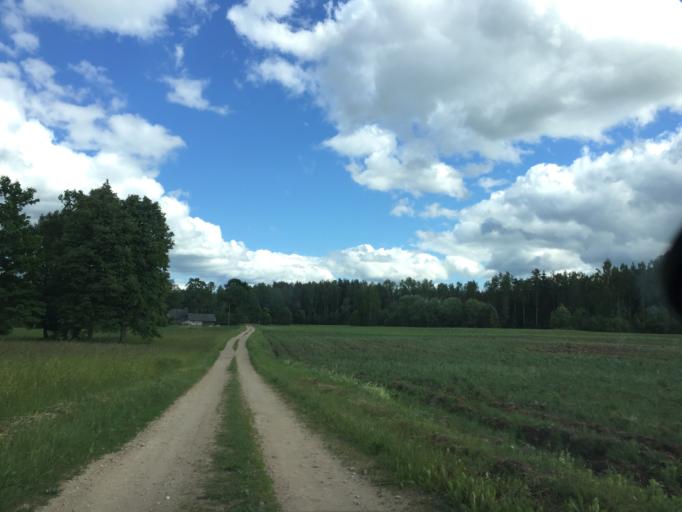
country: LV
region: Vecumnieki
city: Vecumnieki
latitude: 56.4252
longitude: 24.5122
